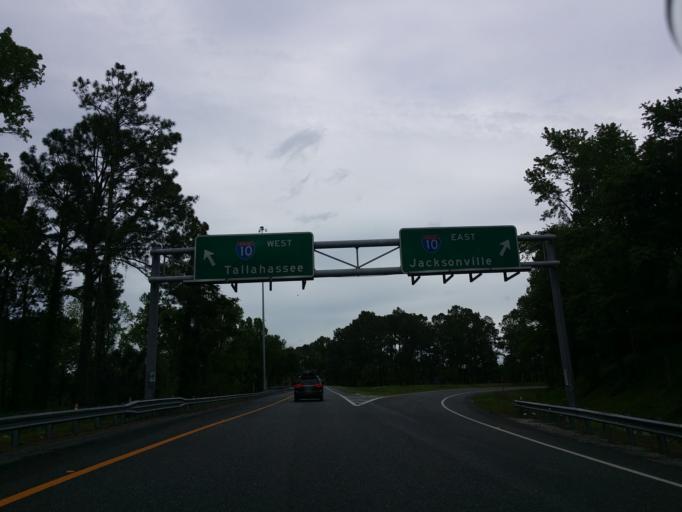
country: US
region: Florida
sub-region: Suwannee County
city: Wellborn
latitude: 30.2635
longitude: -82.7516
